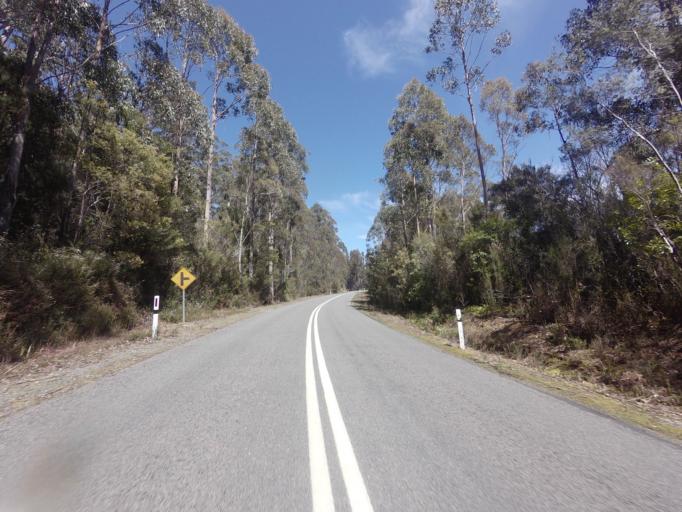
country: AU
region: Tasmania
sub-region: Huon Valley
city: Geeveston
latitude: -42.8301
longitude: 146.2704
